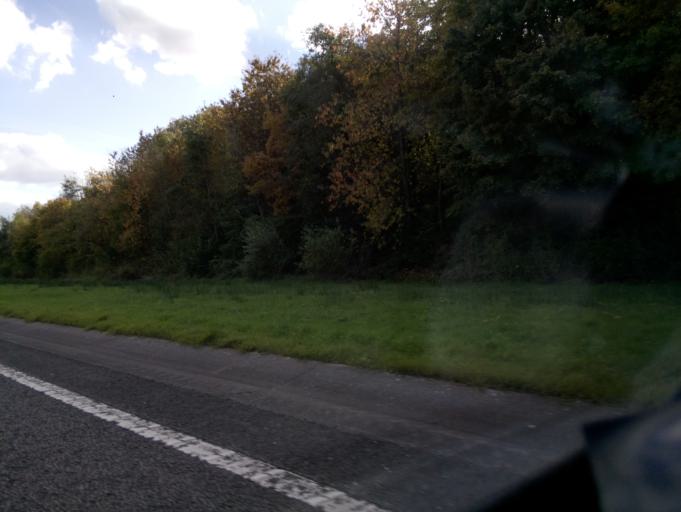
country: GB
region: Wales
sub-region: Merthyr Tydfil County Borough
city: Merthyr Tydfil
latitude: 51.7553
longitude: -3.4004
